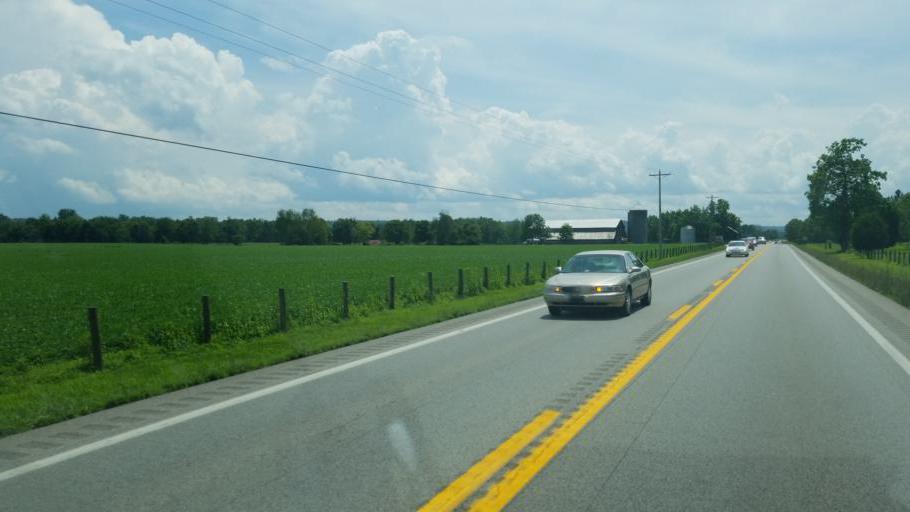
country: US
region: West Virginia
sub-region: Putnam County
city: Buffalo
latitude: 38.6591
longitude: -81.9689
